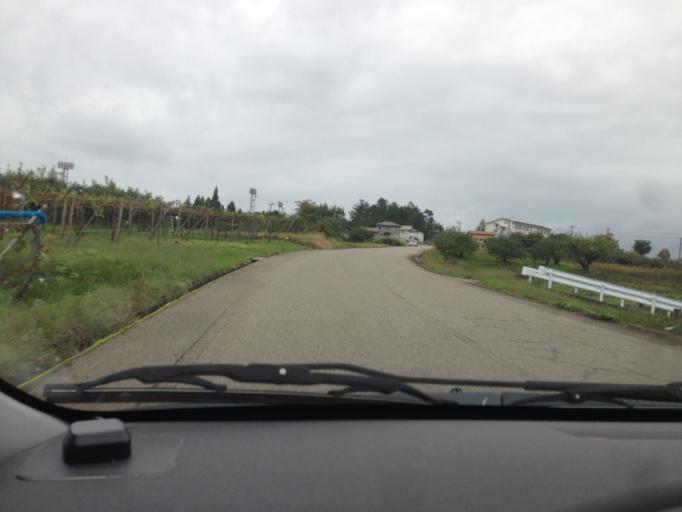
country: JP
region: Fukushima
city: Kitakata
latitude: 37.5046
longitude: 139.8151
